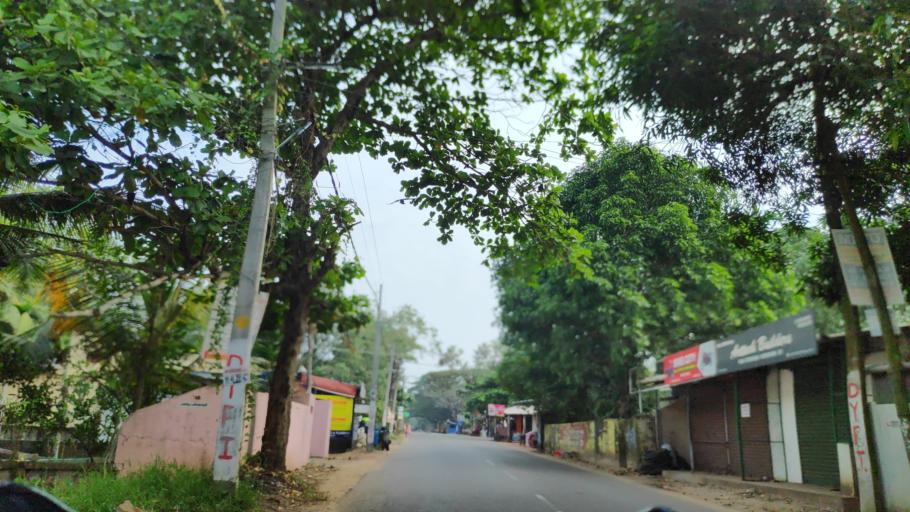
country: IN
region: Kerala
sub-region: Alappuzha
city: Shertallai
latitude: 9.7004
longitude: 76.3513
